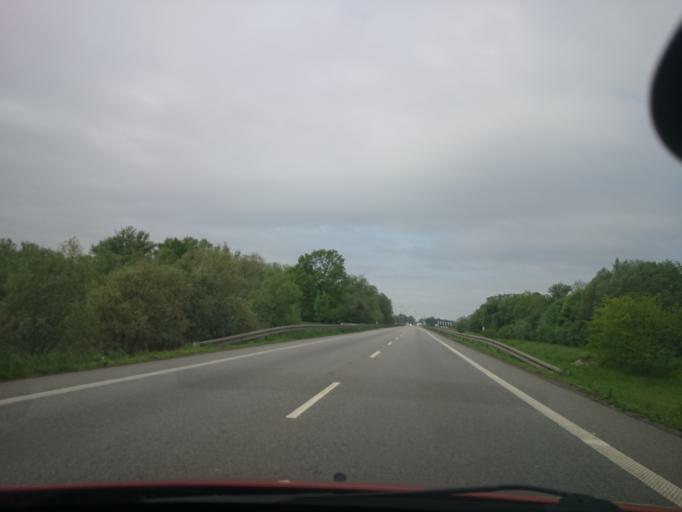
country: PL
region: Opole Voivodeship
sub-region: Powiat opolski
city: Czarnowasy
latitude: 50.6983
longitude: 17.8865
